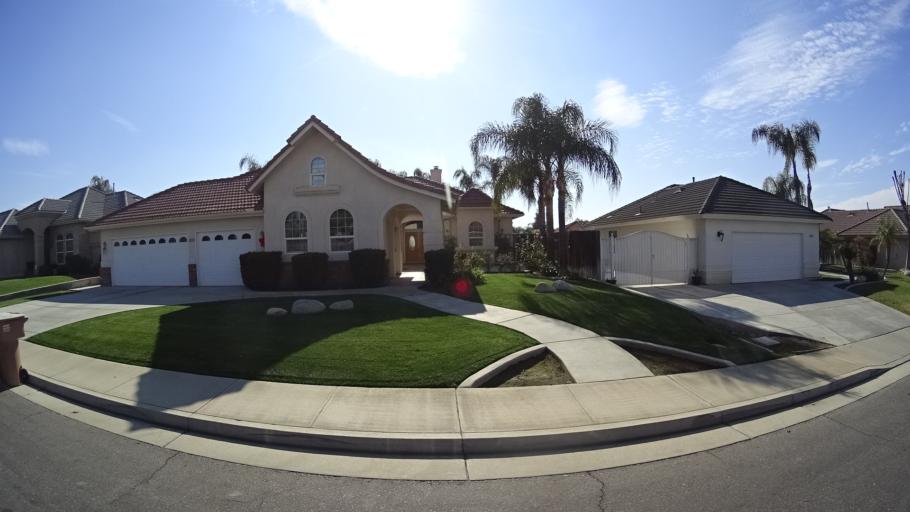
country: US
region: California
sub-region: Kern County
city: Lamont
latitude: 35.3893
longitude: -118.8811
